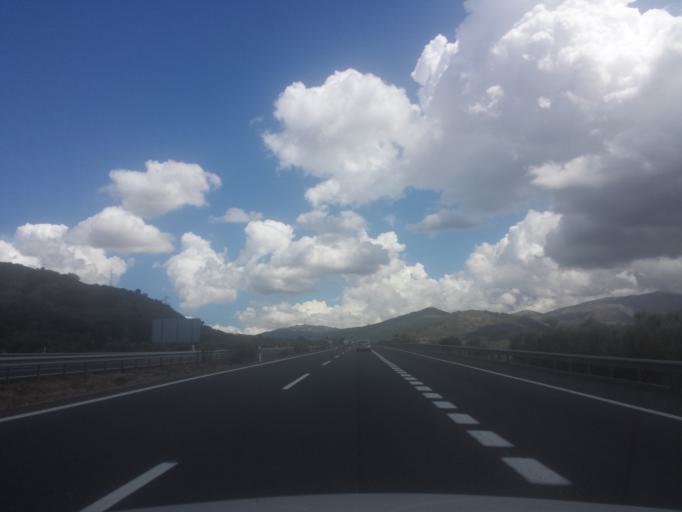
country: ES
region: Extremadura
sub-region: Provincia de Caceres
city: Aldeanueva del Camino
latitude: 40.2762
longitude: -5.9072
